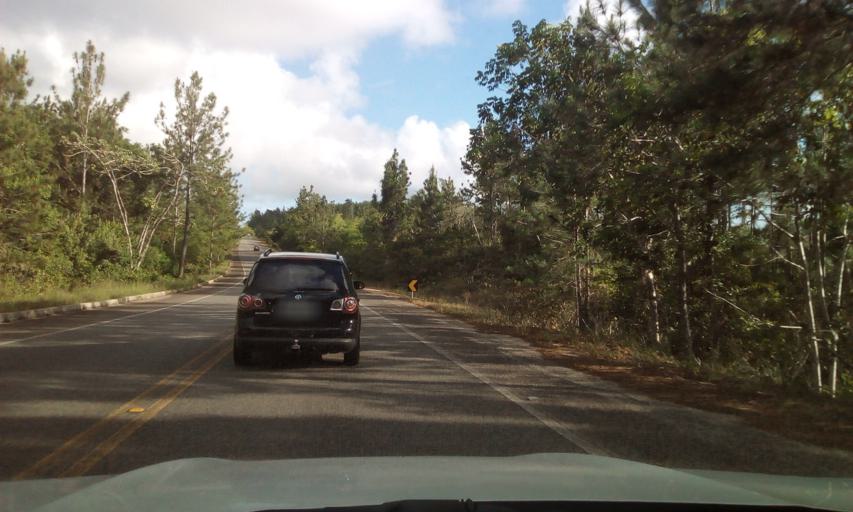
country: BR
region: Bahia
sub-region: Entre Rios
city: Entre Rios
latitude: -12.1393
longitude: -37.7914
